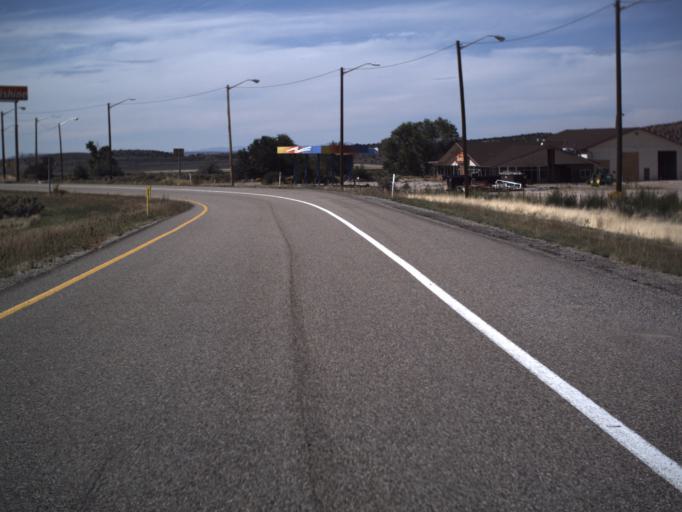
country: US
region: Utah
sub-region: Iron County
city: Enoch
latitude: 37.8043
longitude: -112.9458
